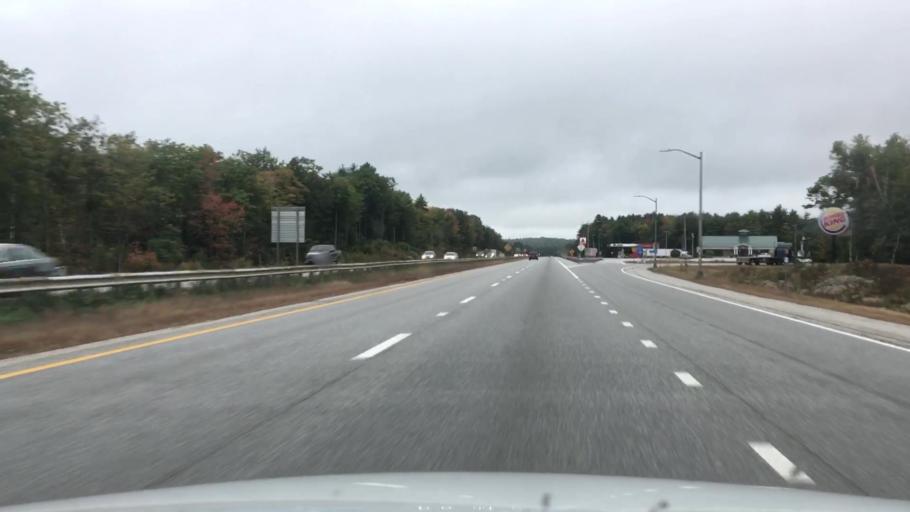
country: US
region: Maine
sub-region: Cumberland County
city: Cumberland Center
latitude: 43.8216
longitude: -70.3200
